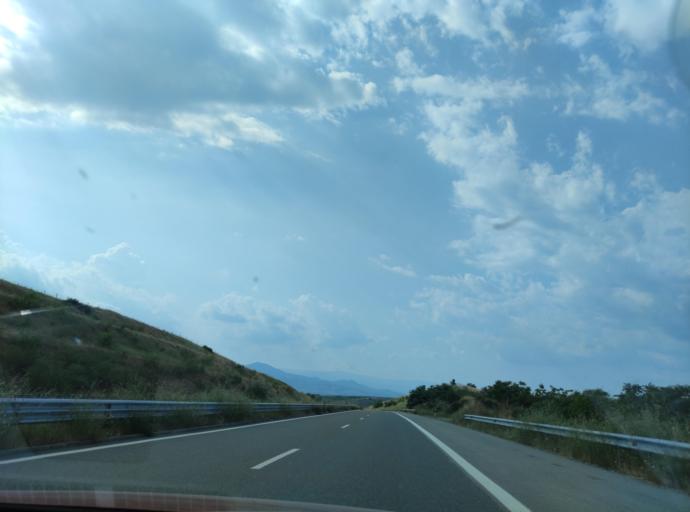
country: BG
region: Blagoevgrad
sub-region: Obshtina Sandanski
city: Sandanski
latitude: 41.4804
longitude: 23.3068
